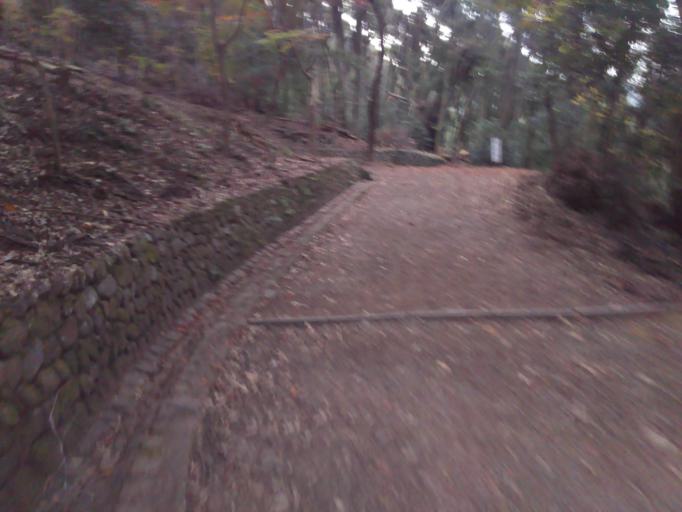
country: JP
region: Kyoto
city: Uji
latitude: 34.8925
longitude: 135.8118
